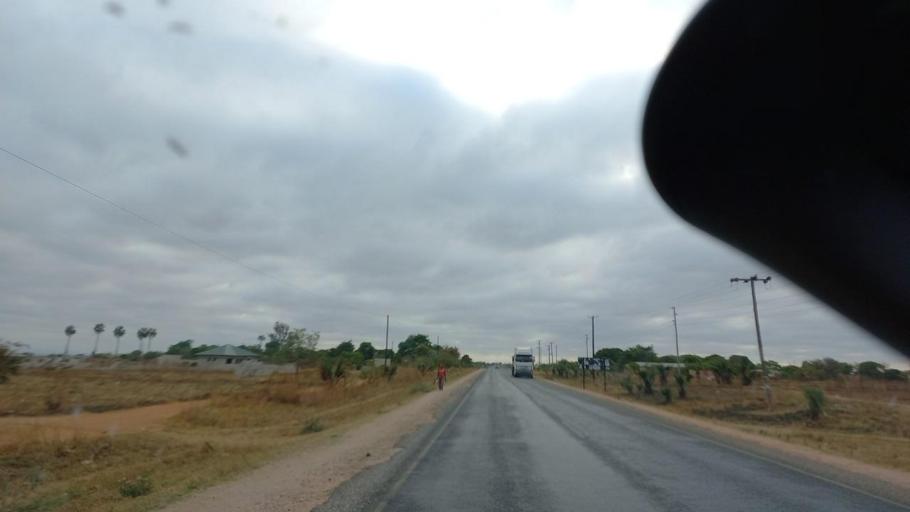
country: ZM
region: Lusaka
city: Chongwe
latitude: -15.3407
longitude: 28.6216
